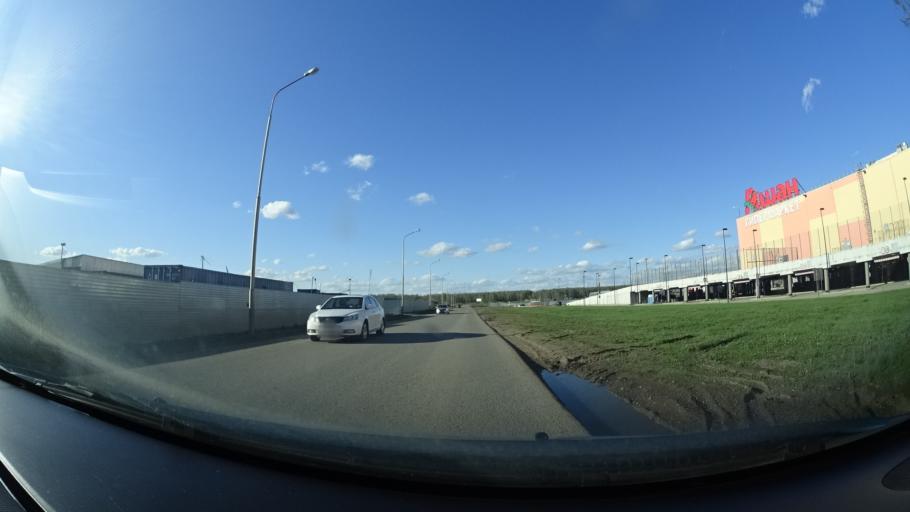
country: RU
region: Bashkortostan
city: Ufa
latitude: 54.6747
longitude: 55.9255
